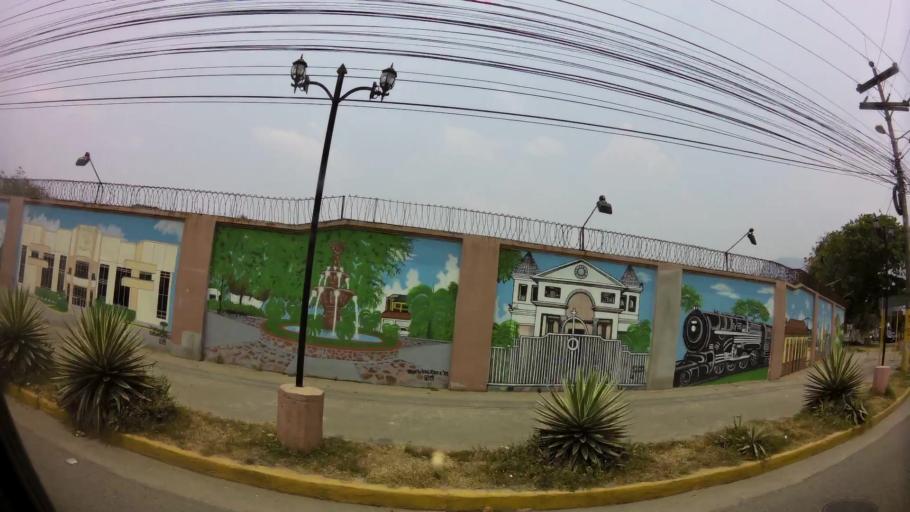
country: HN
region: Yoro
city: El Progreso
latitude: 15.3941
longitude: -87.8079
